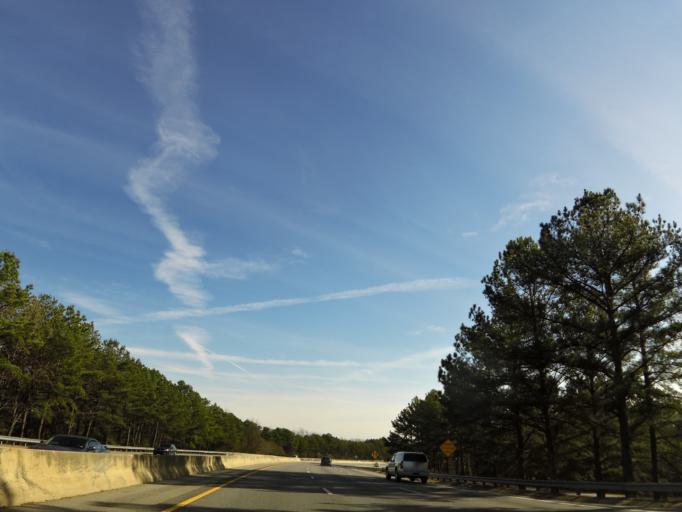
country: US
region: Georgia
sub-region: Muscogee County
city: Columbus
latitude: 32.5186
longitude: -84.9525
